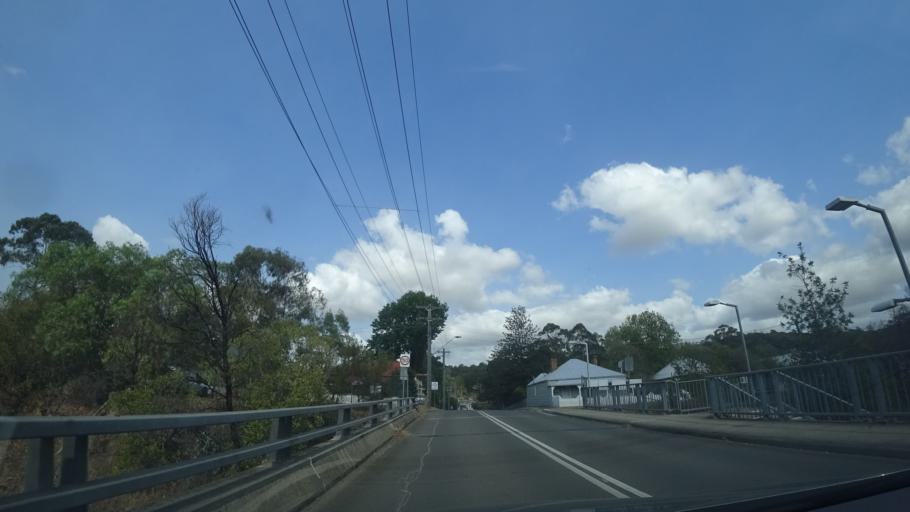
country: AU
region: New South Wales
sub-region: Wollondilly
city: Picton
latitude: -34.1797
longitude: 150.6130
